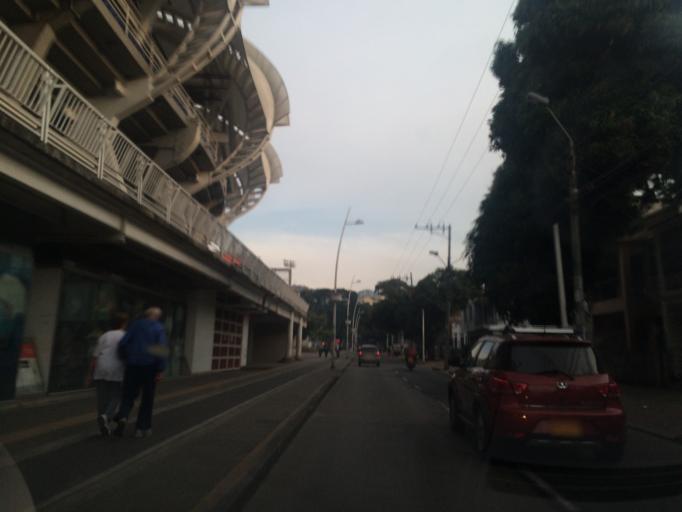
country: CO
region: Valle del Cauca
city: Cali
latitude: 3.4303
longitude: -76.5405
